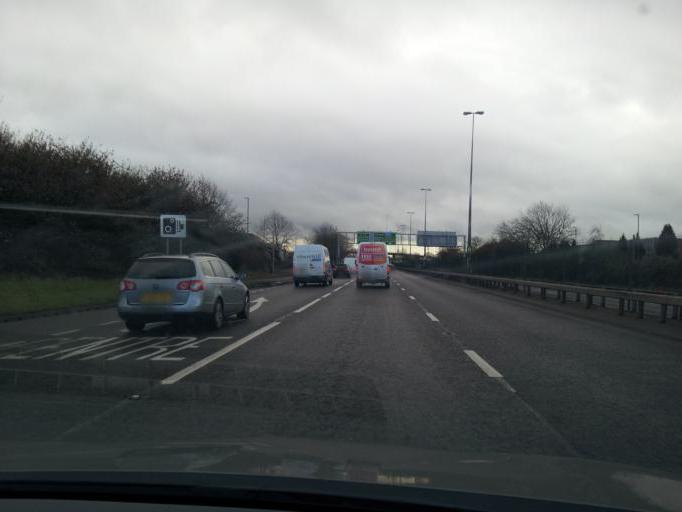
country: GB
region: England
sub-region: Nottingham
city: Nottingham
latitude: 52.9334
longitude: -1.1716
